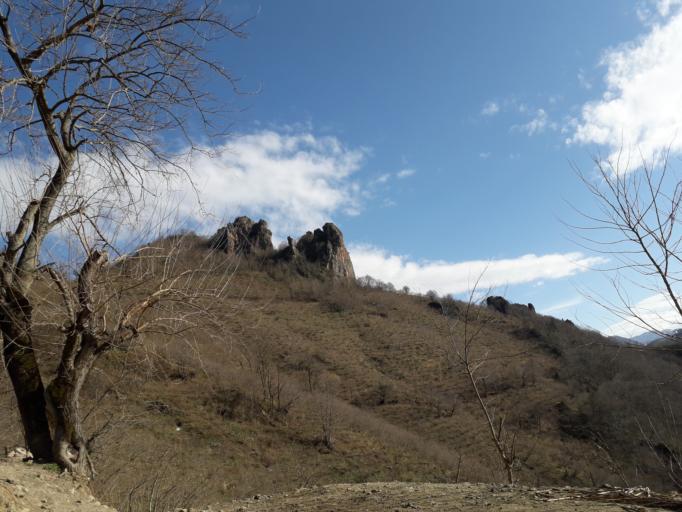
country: TR
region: Ordu
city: Kabaduz
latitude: 40.8894
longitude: 37.8950
